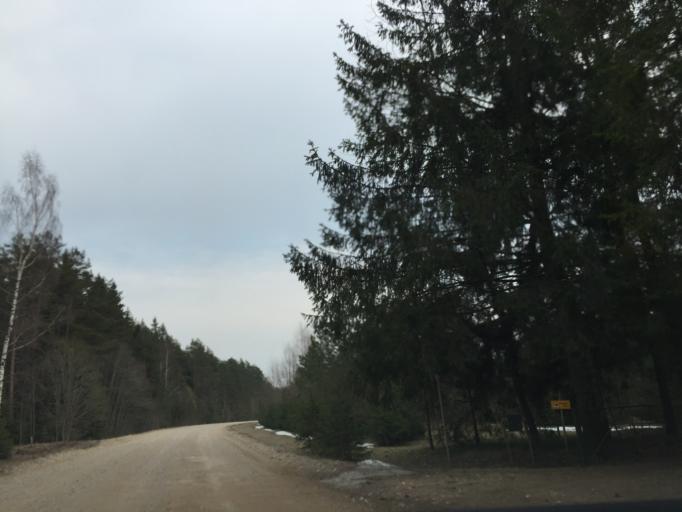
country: LV
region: Raunas
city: Rauna
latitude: 57.1640
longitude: 25.5157
